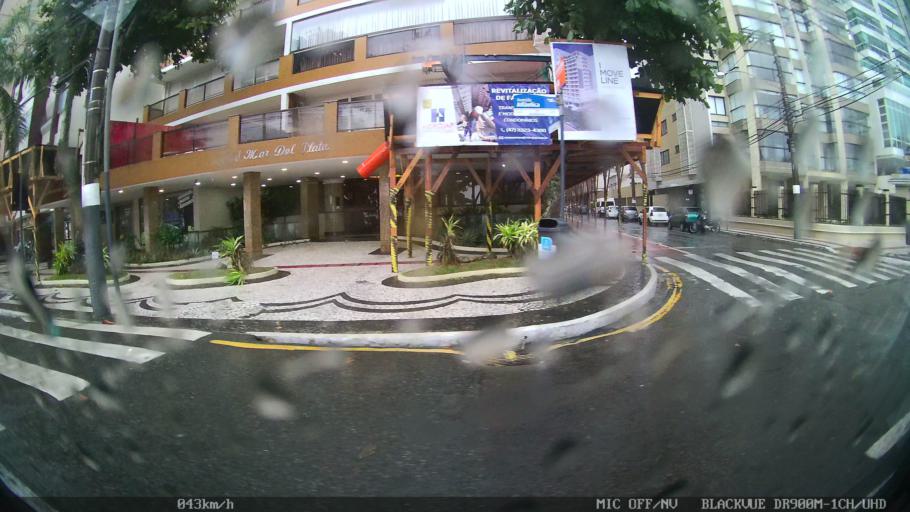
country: BR
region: Santa Catarina
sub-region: Balneario Camboriu
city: Balneario Camboriu
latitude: -26.9767
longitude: -48.6353
